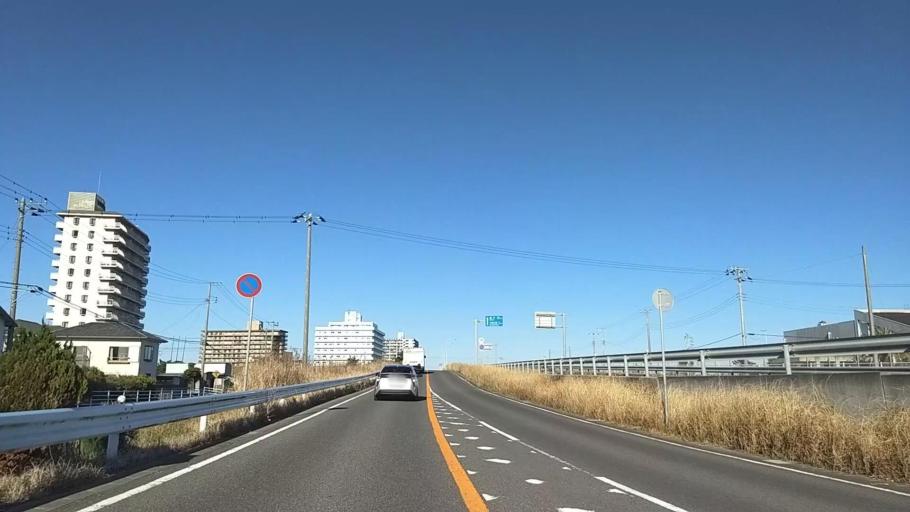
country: JP
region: Chiba
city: Mobara
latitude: 35.4473
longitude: 140.4015
